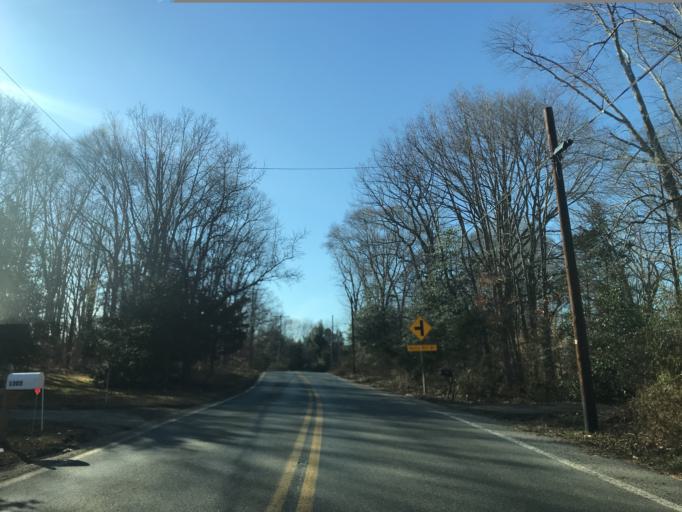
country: US
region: Maryland
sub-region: Prince George's County
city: Accokeek
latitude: 38.6695
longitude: -76.9853
